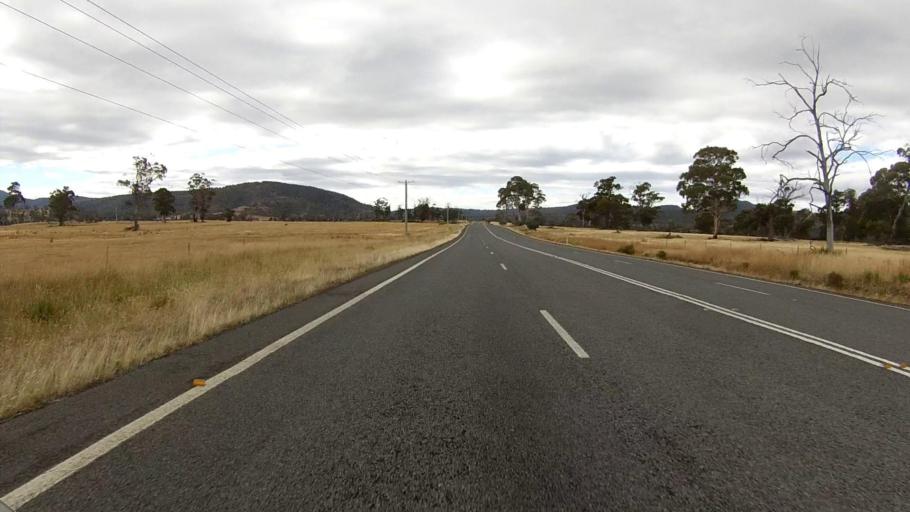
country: AU
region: Tasmania
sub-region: Sorell
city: Sorell
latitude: -42.5989
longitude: 147.7633
